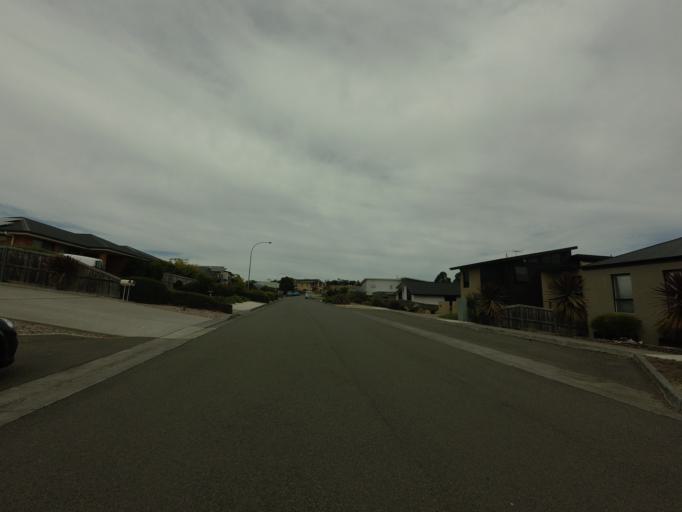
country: AU
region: Tasmania
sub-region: Sorell
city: Sorell
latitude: -42.7845
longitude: 147.5246
